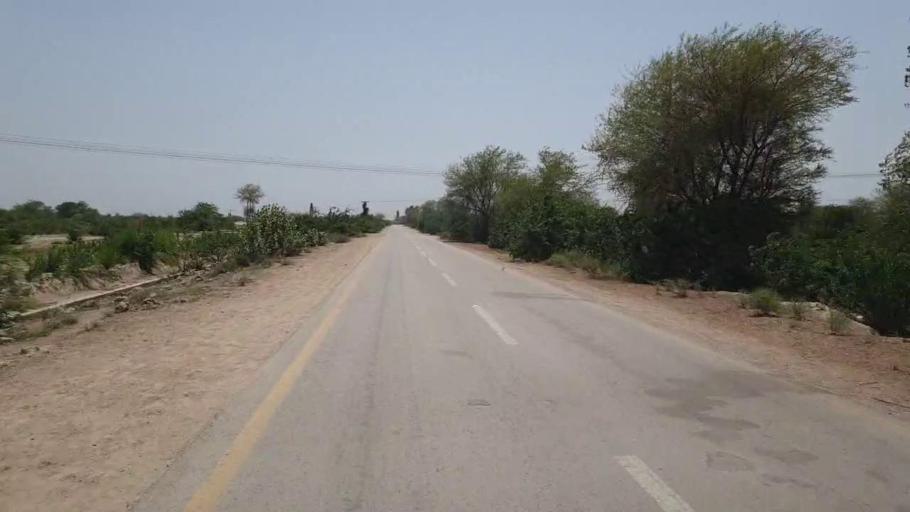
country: PK
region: Sindh
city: Daur
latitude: 26.3454
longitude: 68.1304
